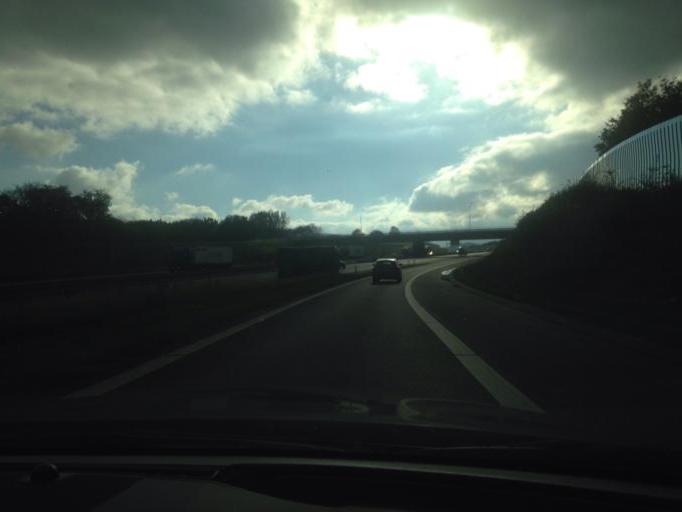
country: DK
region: South Denmark
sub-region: Vejle Kommune
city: Vejle
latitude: 55.6829
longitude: 9.5625
